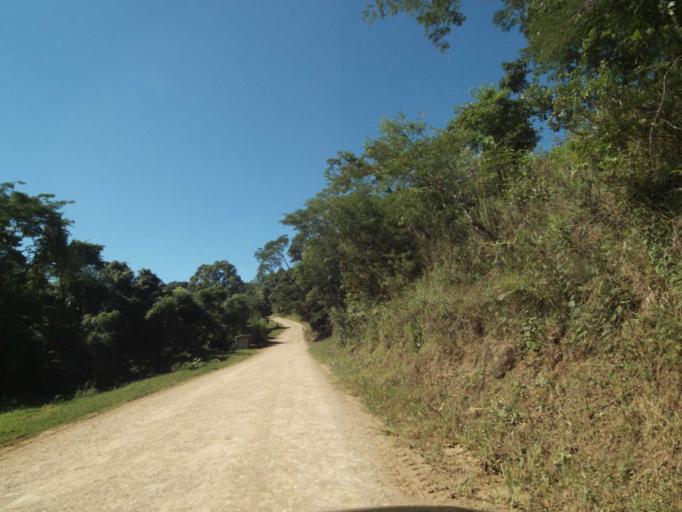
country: BR
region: Parana
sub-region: Francisco Beltrao
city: Francisco Beltrao
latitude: -26.1477
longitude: -53.3041
